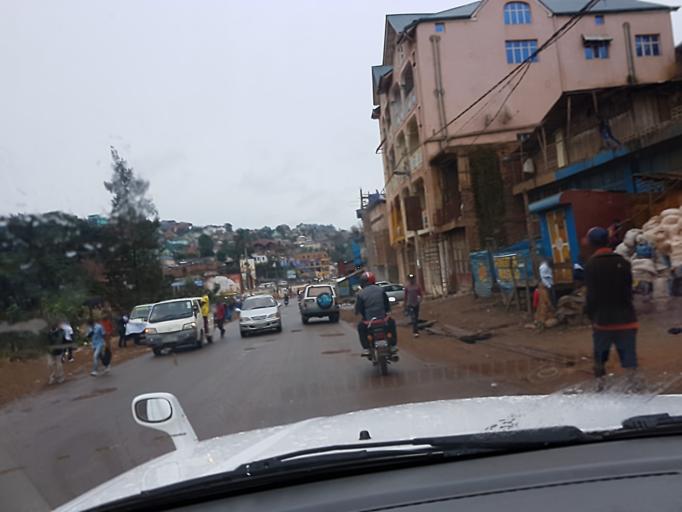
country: CD
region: South Kivu
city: Bukavu
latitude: -2.4991
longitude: 28.8510
